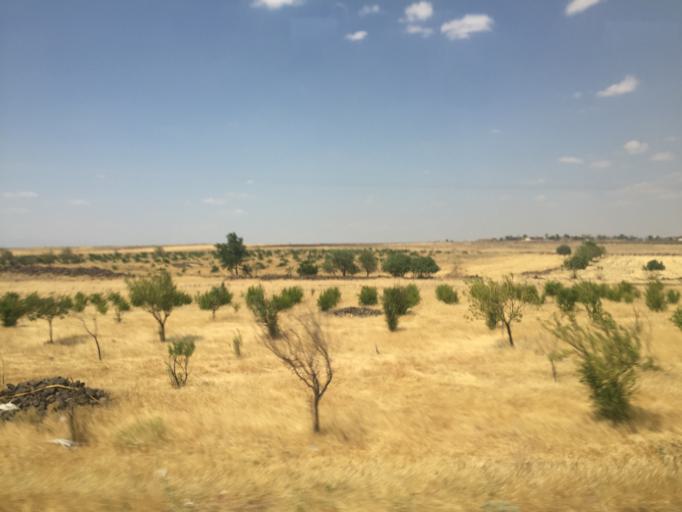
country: TR
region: Sanliurfa
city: Siverek
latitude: 37.7724
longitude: 39.4452
